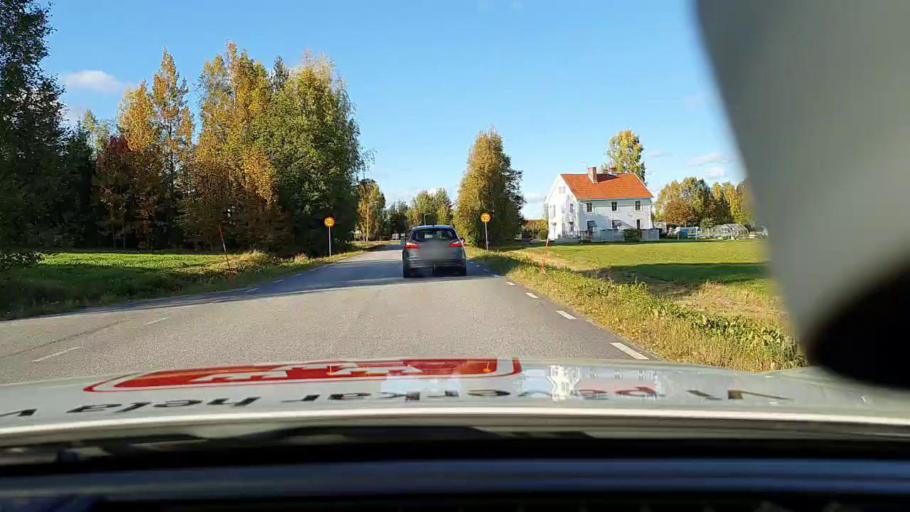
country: SE
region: Norrbotten
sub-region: Pitea Kommun
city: Norrfjarden
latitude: 65.5151
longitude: 21.4954
